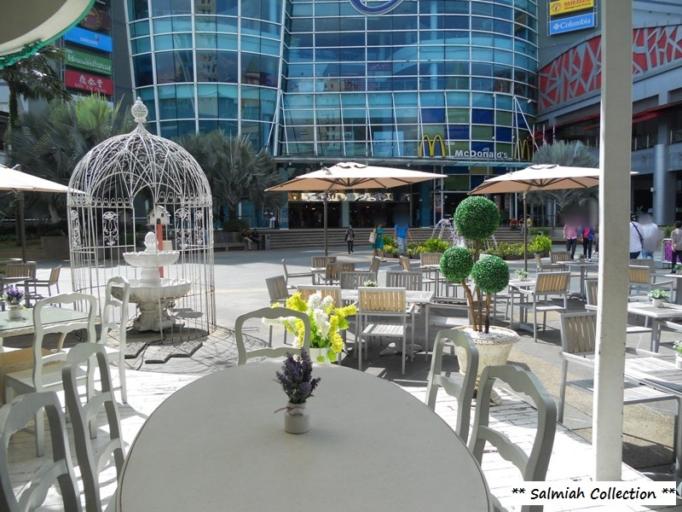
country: MY
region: Selangor
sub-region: Petaling
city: Petaling Jaya
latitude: 3.1569
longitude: 101.6104
